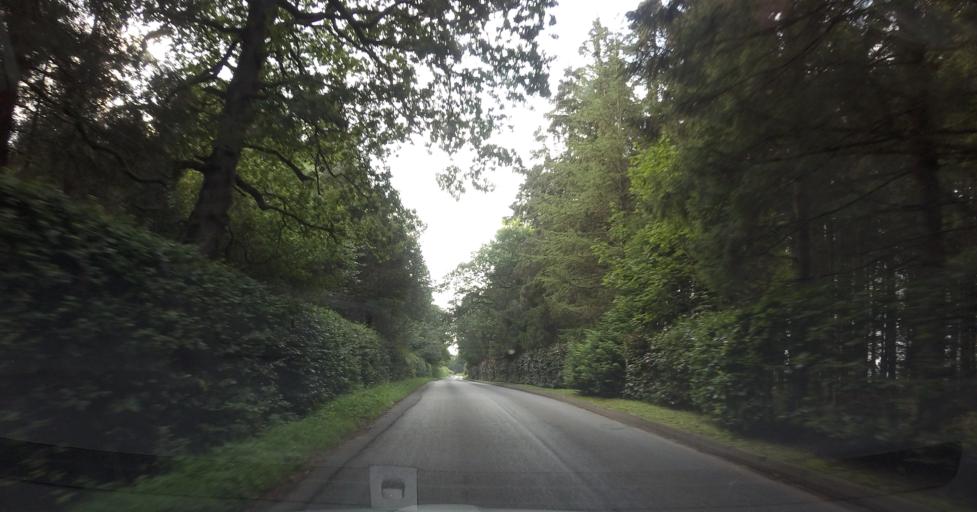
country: GB
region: Scotland
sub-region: Perth and Kinross
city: Auchterarder
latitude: 56.3070
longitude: -3.7303
